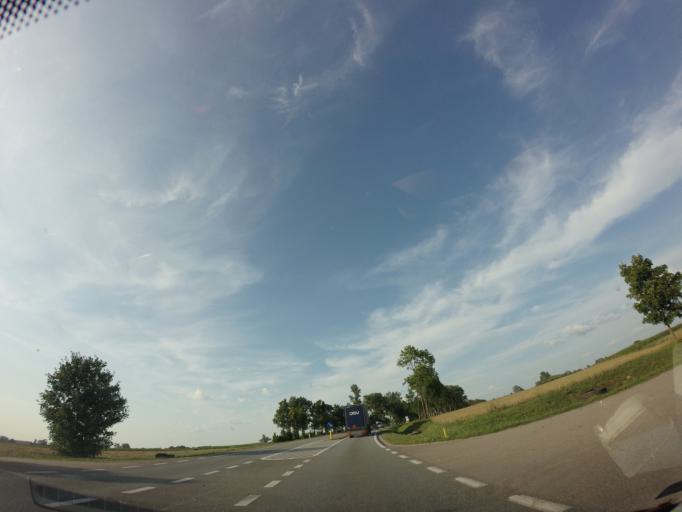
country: PL
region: Podlasie
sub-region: Powiat sokolski
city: Suchowola
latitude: 53.5096
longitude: 23.0996
